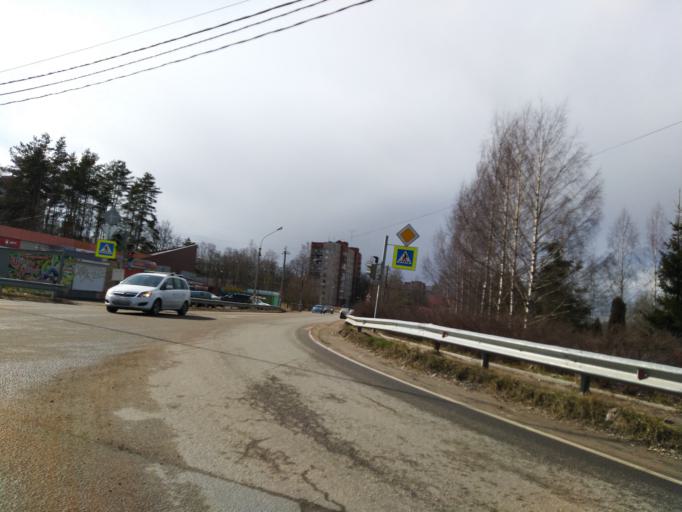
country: RU
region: Leningrad
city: Toksovo
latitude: 60.1118
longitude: 30.5010
